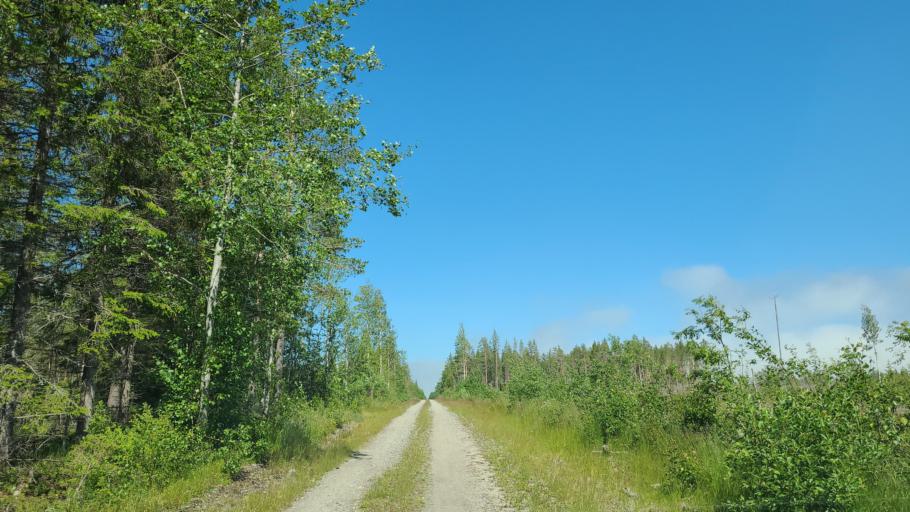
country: SE
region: Vaesternorrland
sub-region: OErnskoeldsviks Kommun
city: Husum
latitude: 63.4311
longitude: 19.2287
